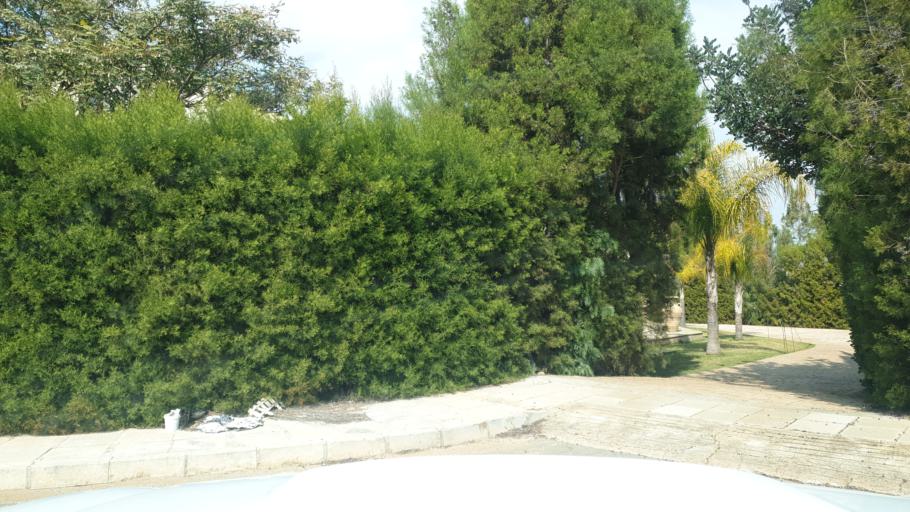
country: CY
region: Lefkosia
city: Kato Deftera
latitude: 35.0813
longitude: 33.2885
